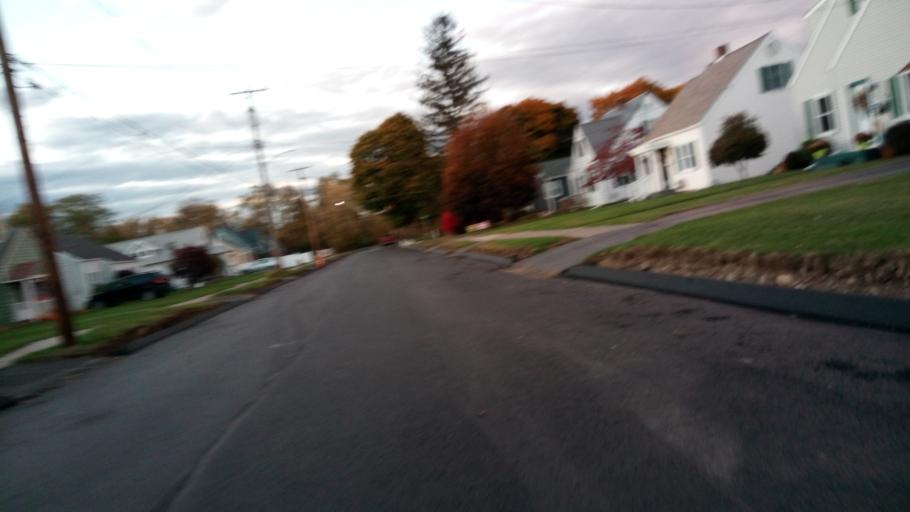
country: US
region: New York
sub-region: Chemung County
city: Elmira
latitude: 42.0772
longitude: -76.8183
